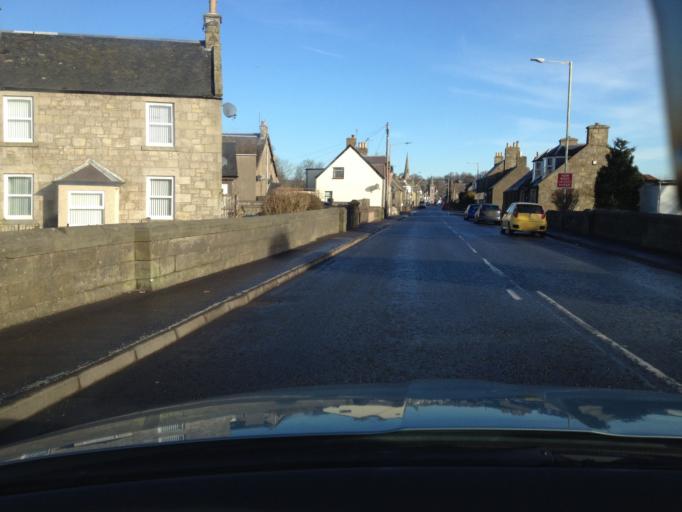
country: GB
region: Scotland
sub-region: Perth and Kinross
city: Milnathort
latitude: 56.2225
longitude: -3.4239
